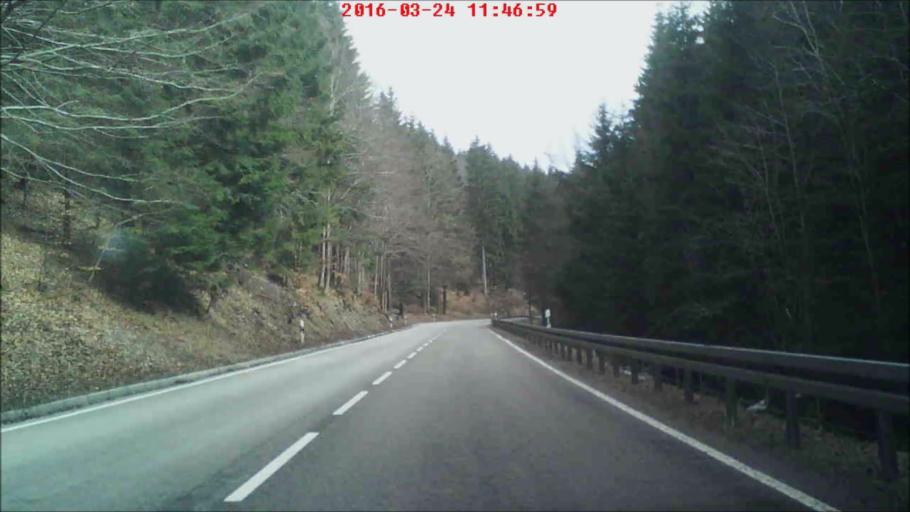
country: DE
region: Thuringia
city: Bachfeld
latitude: 50.4588
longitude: 11.0099
